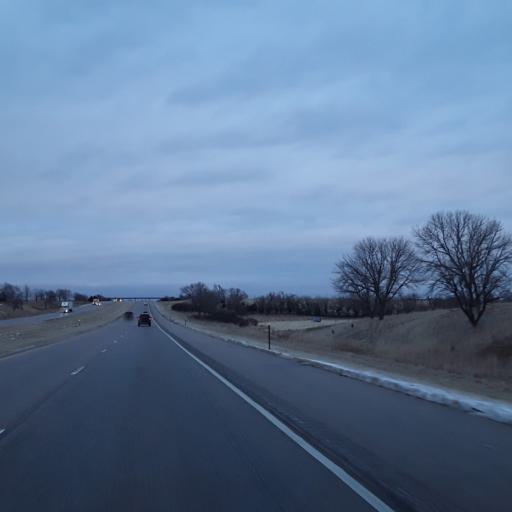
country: US
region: Nebraska
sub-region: Saline County
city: Friend
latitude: 40.8222
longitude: -97.2681
